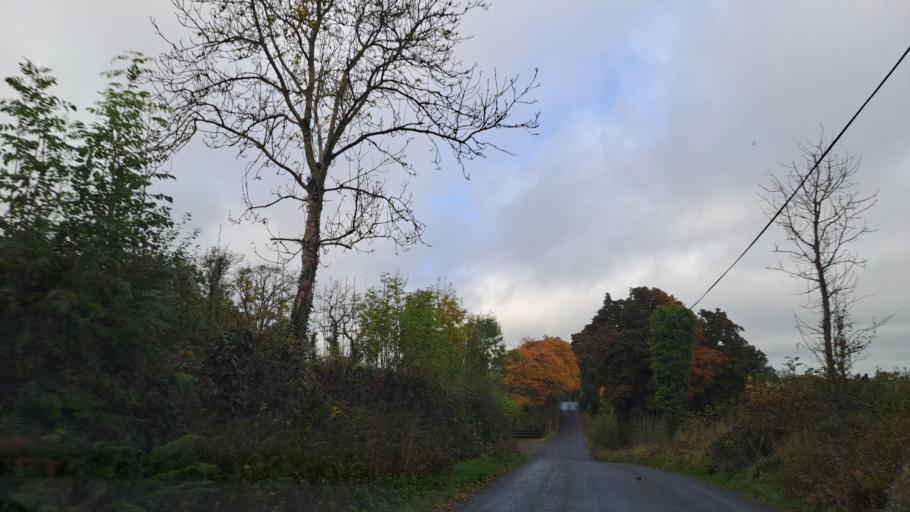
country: IE
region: Ulster
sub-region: An Cabhan
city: Bailieborough
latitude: 53.9892
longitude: -7.0019
